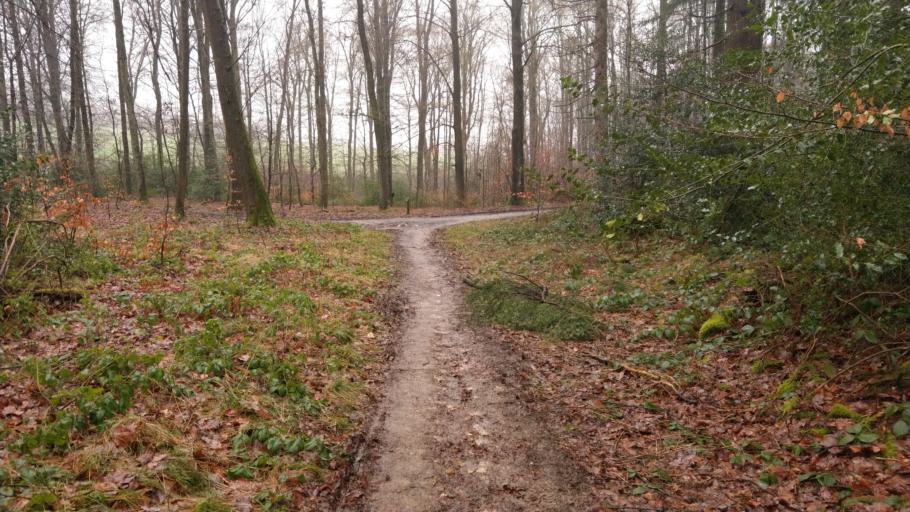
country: NL
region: Limburg
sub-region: Gemeente Vaals
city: Vaals
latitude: 50.7502
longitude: 6.0341
